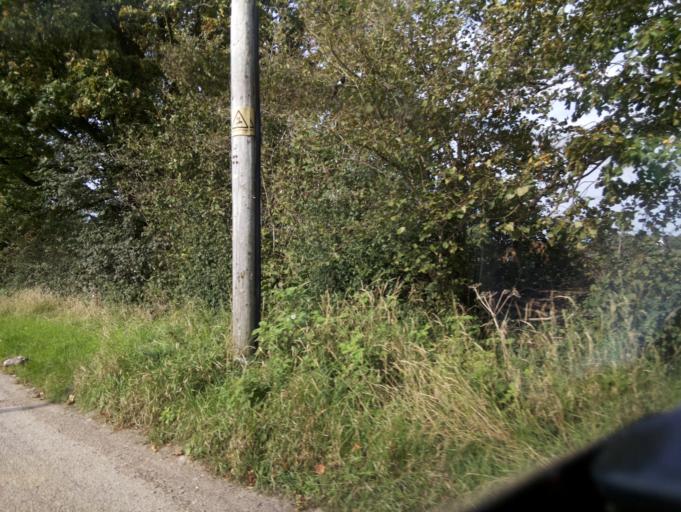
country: GB
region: England
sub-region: South Gloucestershire
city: Alveston
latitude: 51.5846
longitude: -2.5290
